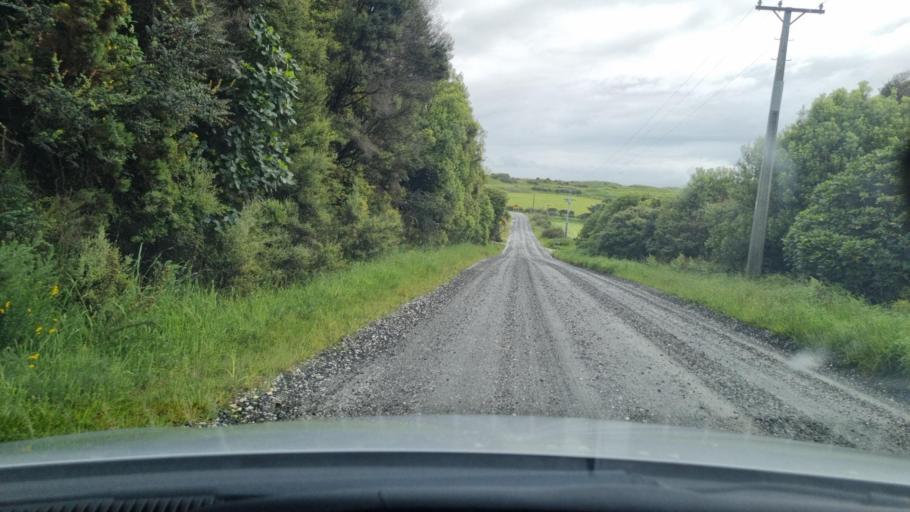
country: NZ
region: Southland
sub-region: Invercargill City
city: Bluff
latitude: -46.5229
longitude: 168.2715
